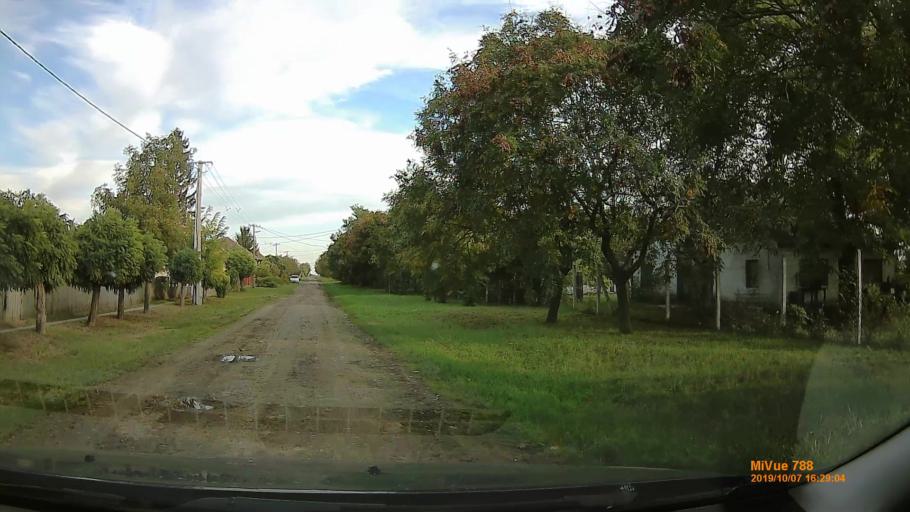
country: HU
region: Bekes
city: Szarvas
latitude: 46.8197
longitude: 20.6496
